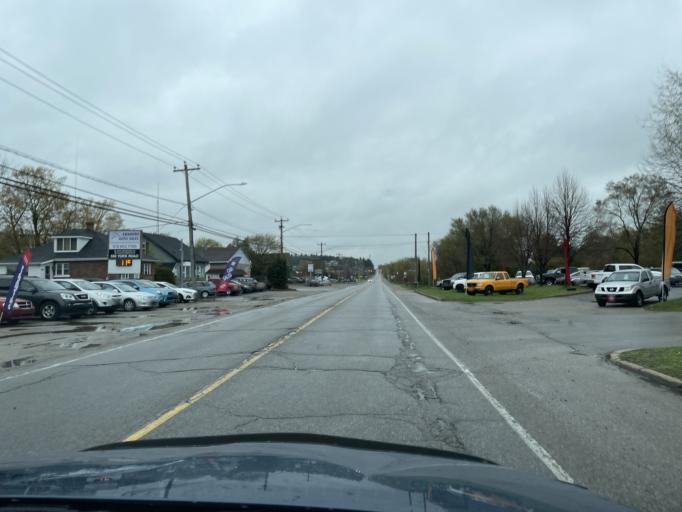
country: CA
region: Ontario
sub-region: Wellington County
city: Guelph
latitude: 43.5537
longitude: -80.2214
